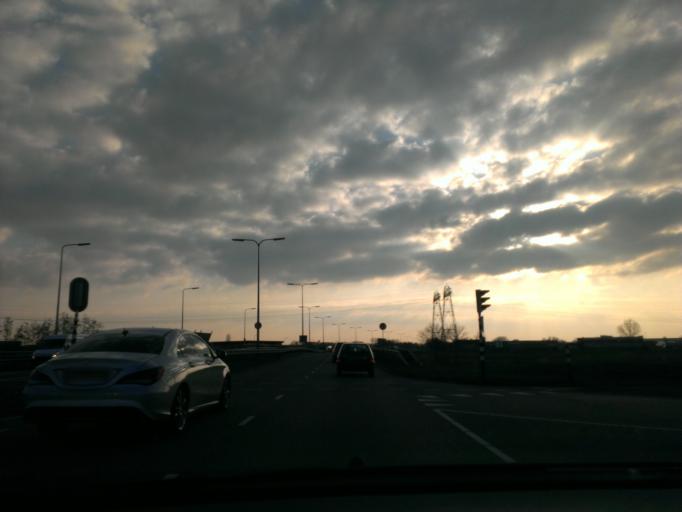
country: NL
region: Overijssel
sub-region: Gemeente Zwolle
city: Zwolle
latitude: 52.4937
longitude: 6.1350
